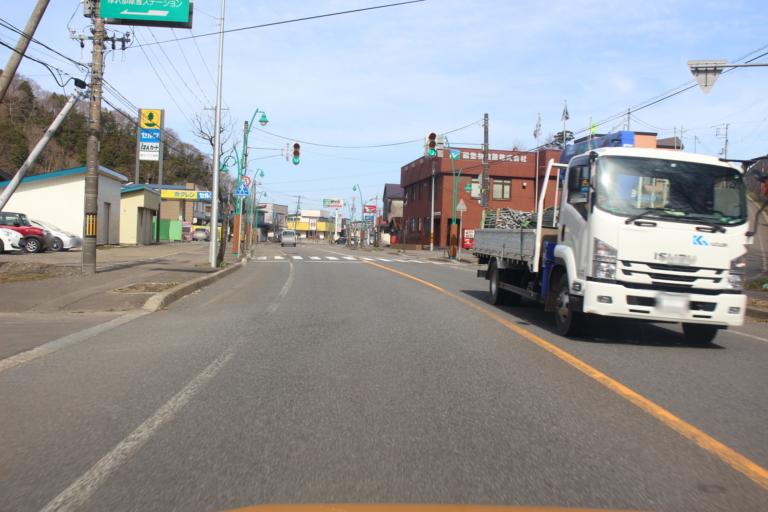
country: JP
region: Hokkaido
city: Kamiiso
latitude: 41.9150
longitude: 140.2270
